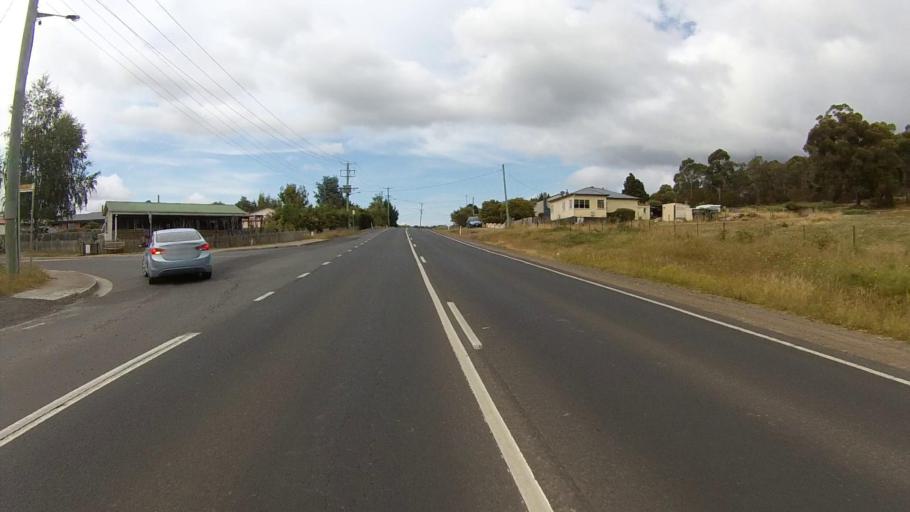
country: AU
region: Tasmania
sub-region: Kingborough
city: Margate
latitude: -43.0514
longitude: 147.2624
